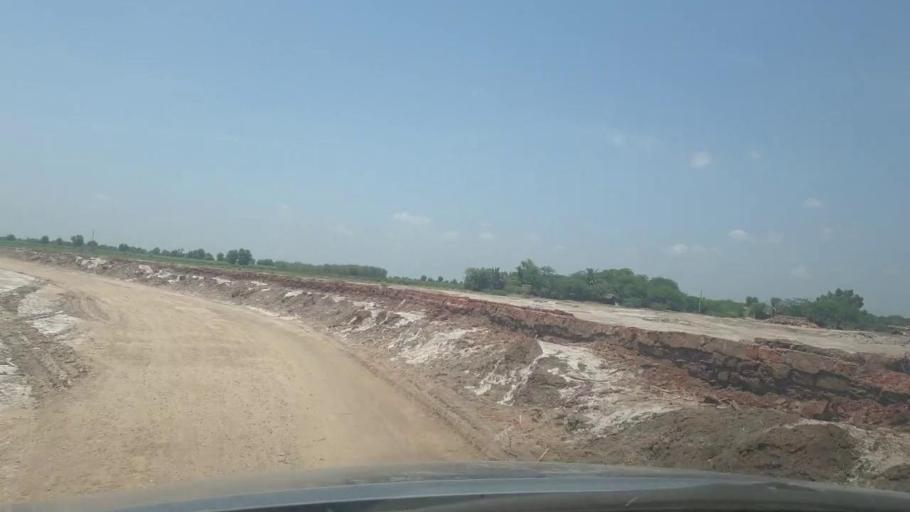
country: PK
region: Sindh
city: Kot Diji
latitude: 27.3873
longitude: 68.6964
